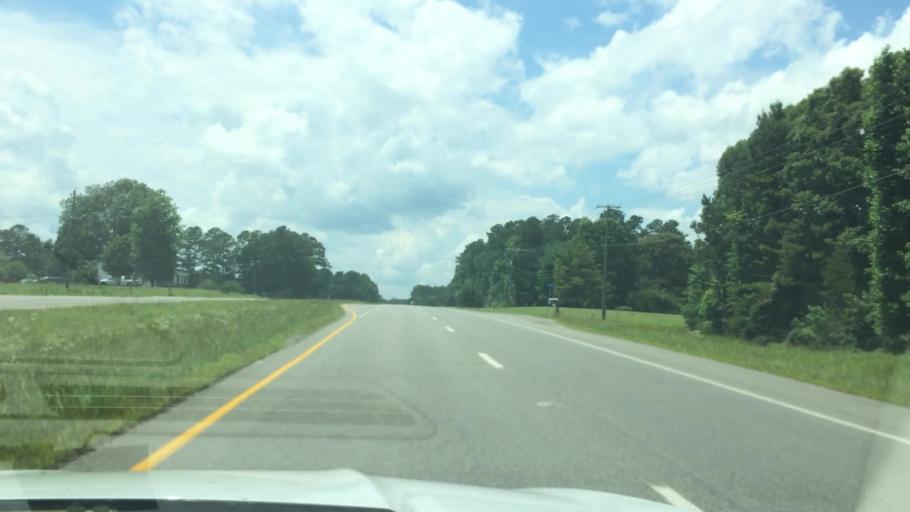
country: US
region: Virginia
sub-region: Middlesex County
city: Saluda
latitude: 37.5627
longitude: -76.6308
